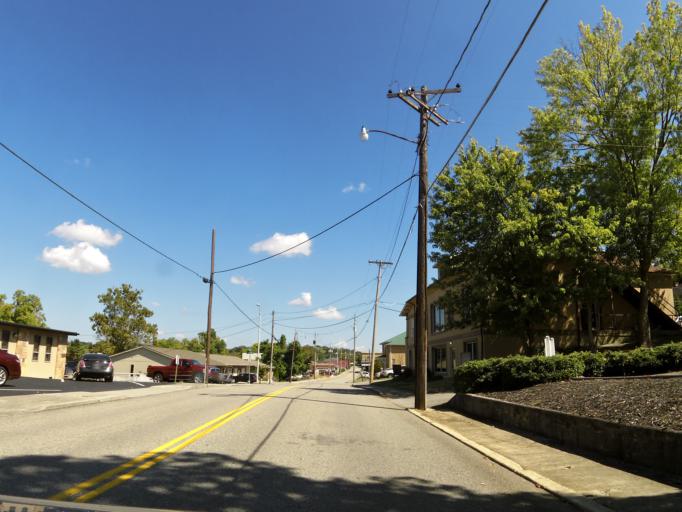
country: US
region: Tennessee
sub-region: Blount County
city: Maryville
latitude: 35.7554
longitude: -83.9688
